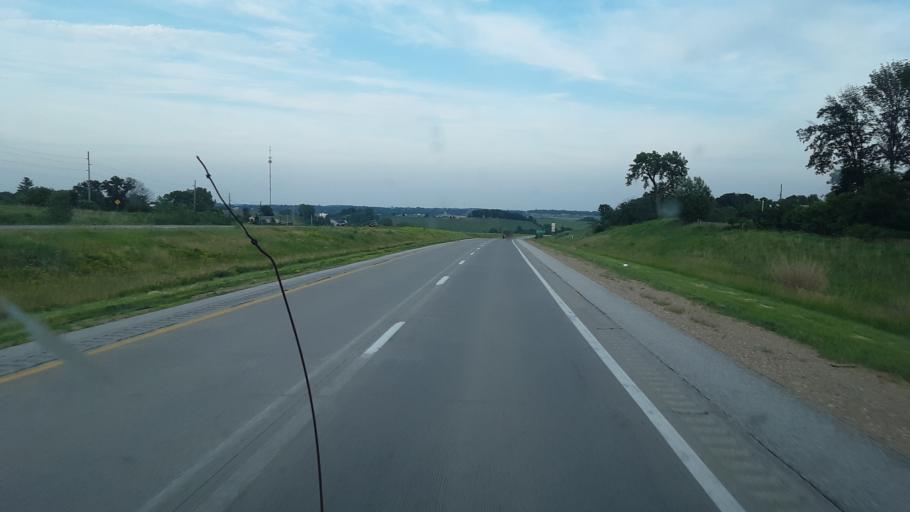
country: US
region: Iowa
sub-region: Tama County
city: Toledo
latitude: 41.9936
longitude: -92.6216
